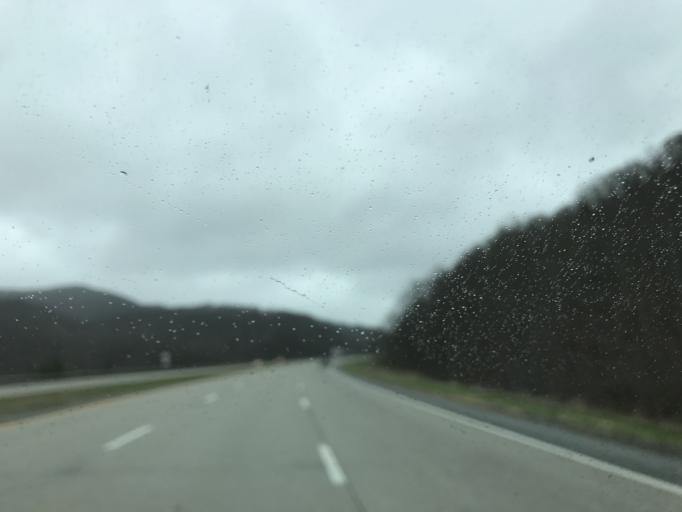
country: US
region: West Virginia
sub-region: Greenbrier County
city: Rainelle
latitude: 37.8293
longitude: -80.7973
